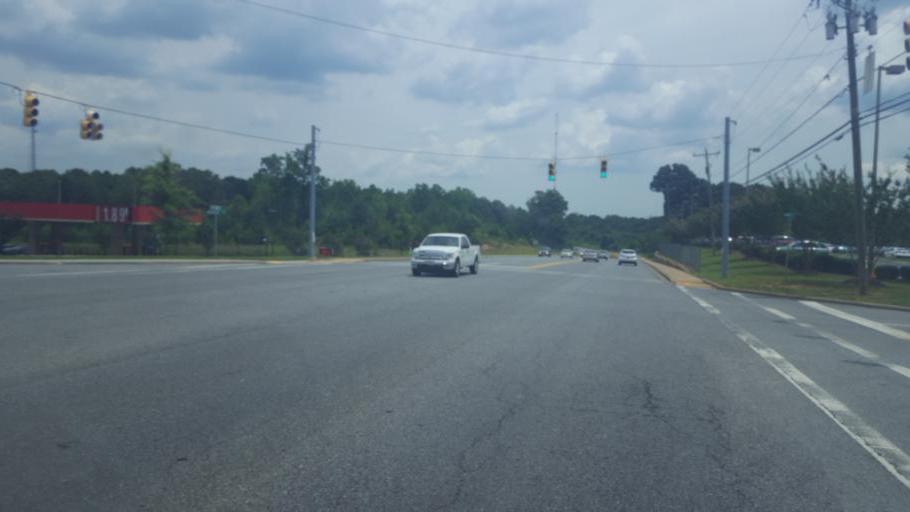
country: US
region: South Carolina
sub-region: York County
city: York
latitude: 34.9851
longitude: -81.2110
